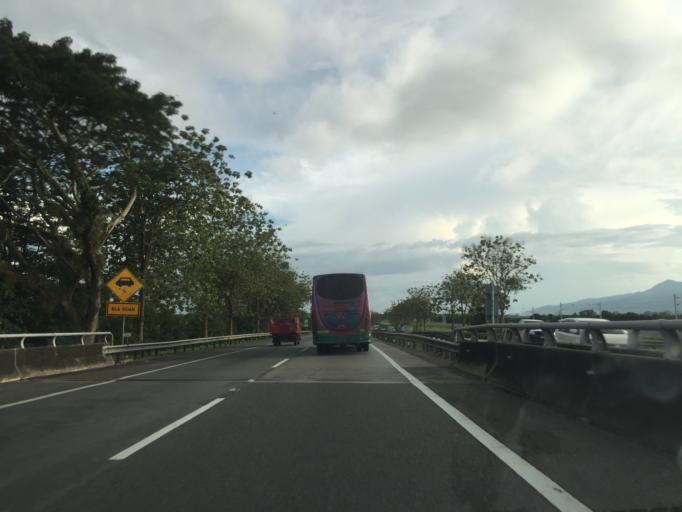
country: MY
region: Kedah
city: Gurun
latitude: 5.8996
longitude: 100.4747
